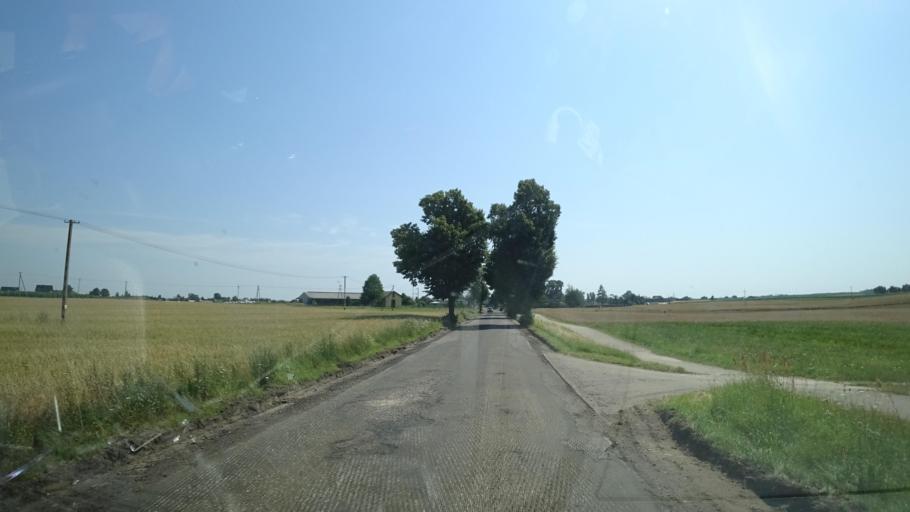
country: PL
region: Pomeranian Voivodeship
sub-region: Powiat chojnicki
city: Brusy
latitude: 53.8722
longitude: 17.6657
